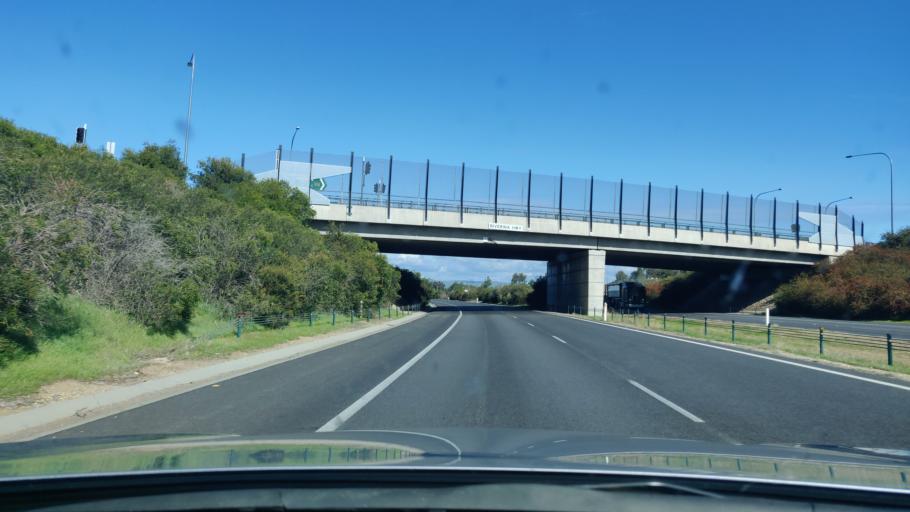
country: AU
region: New South Wales
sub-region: Albury Municipality
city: Albury
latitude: -36.0749
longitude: 146.9284
